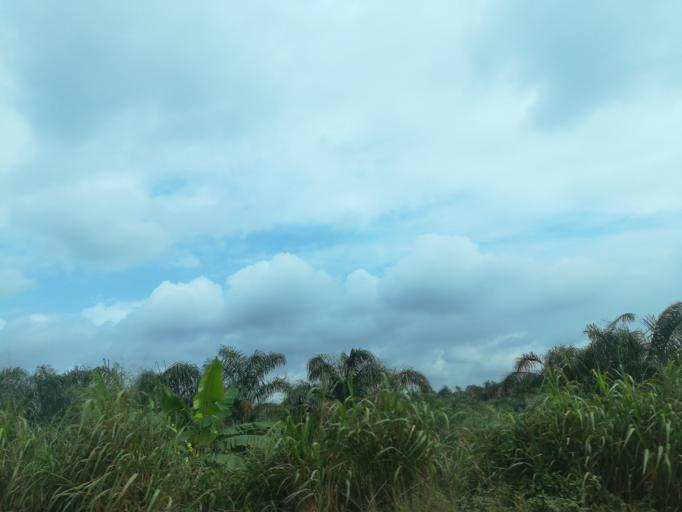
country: NG
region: Lagos
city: Ikorodu
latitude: 6.6478
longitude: 3.5716
